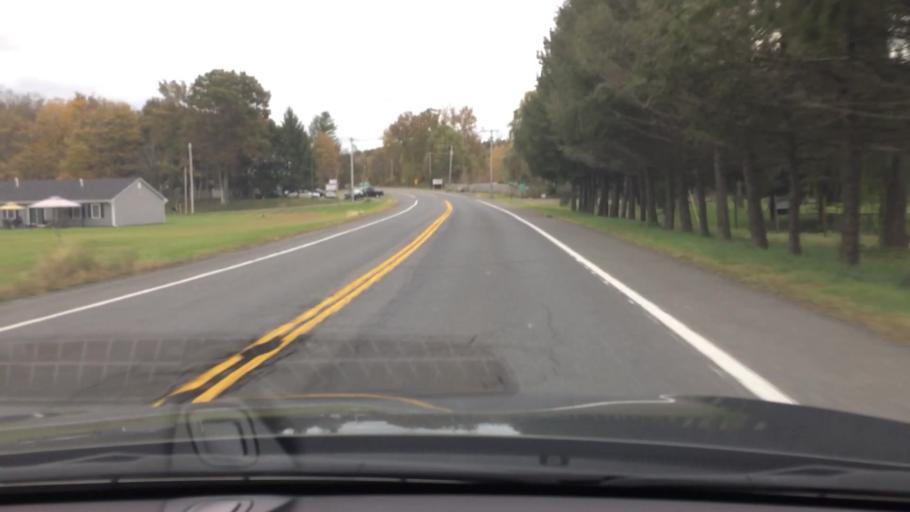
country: US
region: New York
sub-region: Columbia County
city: Oakdale
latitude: 42.1466
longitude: -73.7448
